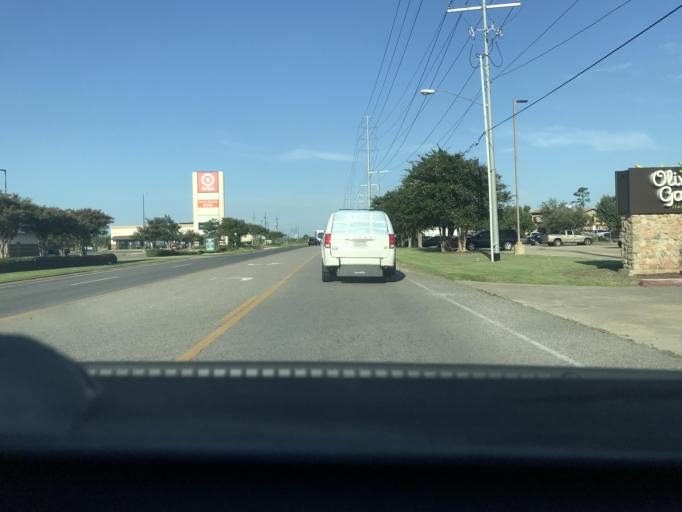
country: US
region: Louisiana
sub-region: Calcasieu Parish
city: Prien
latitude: 30.1977
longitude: -93.2477
